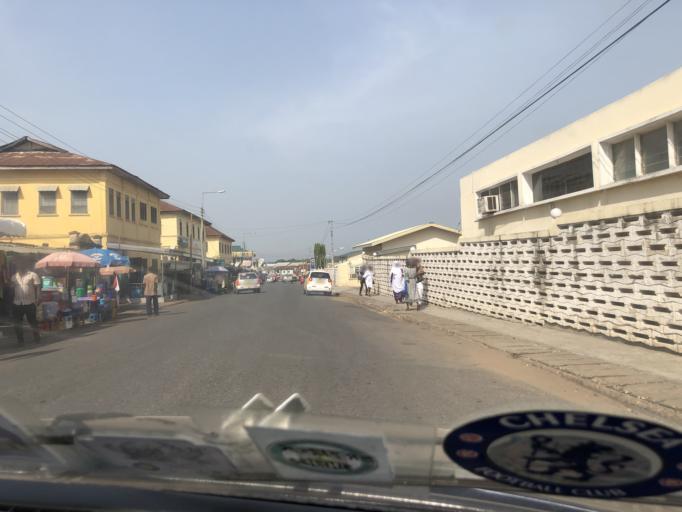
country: GH
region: Eastern
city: Koforidua
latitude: 6.0968
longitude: -0.2569
